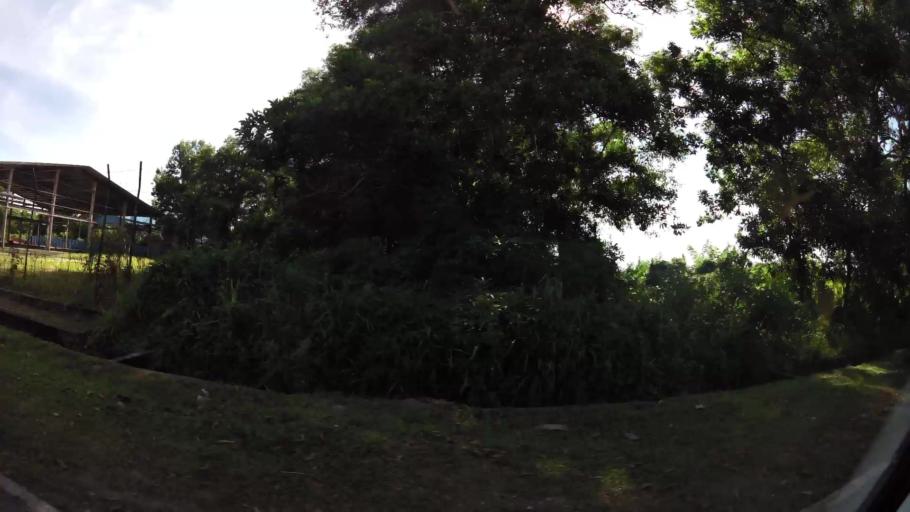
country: BN
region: Belait
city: Kuala Belait
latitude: 4.5734
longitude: 114.2047
